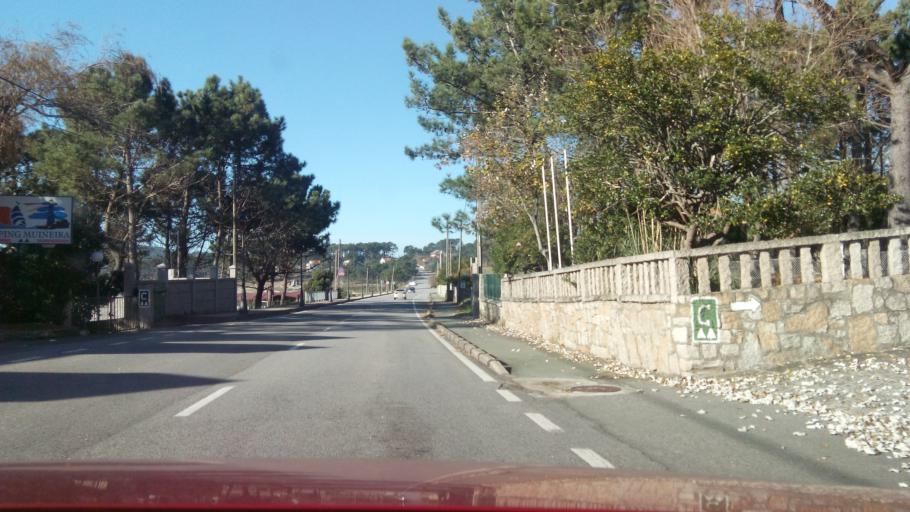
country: ES
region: Galicia
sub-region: Provincia de Pontevedra
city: O Grove
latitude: 42.4601
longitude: -8.8935
